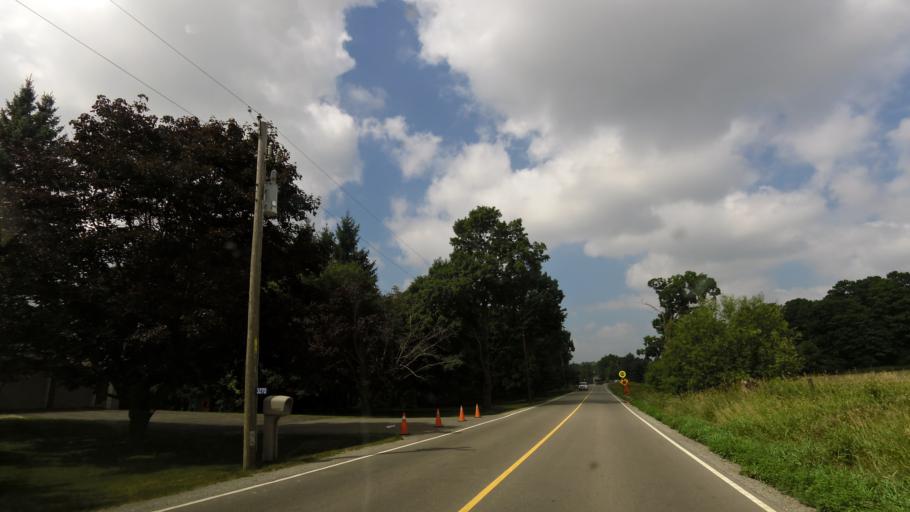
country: CA
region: Ontario
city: Oshawa
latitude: 43.9895
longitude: -78.8714
